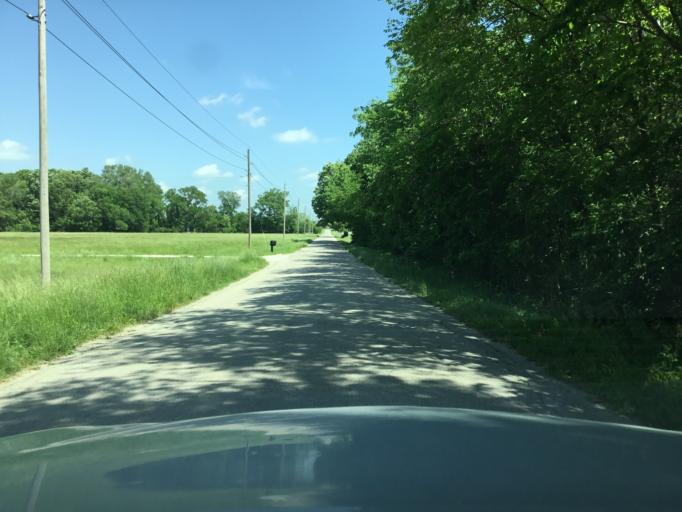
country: US
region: Kansas
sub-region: Labette County
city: Parsons
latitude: 37.3493
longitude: -95.2496
